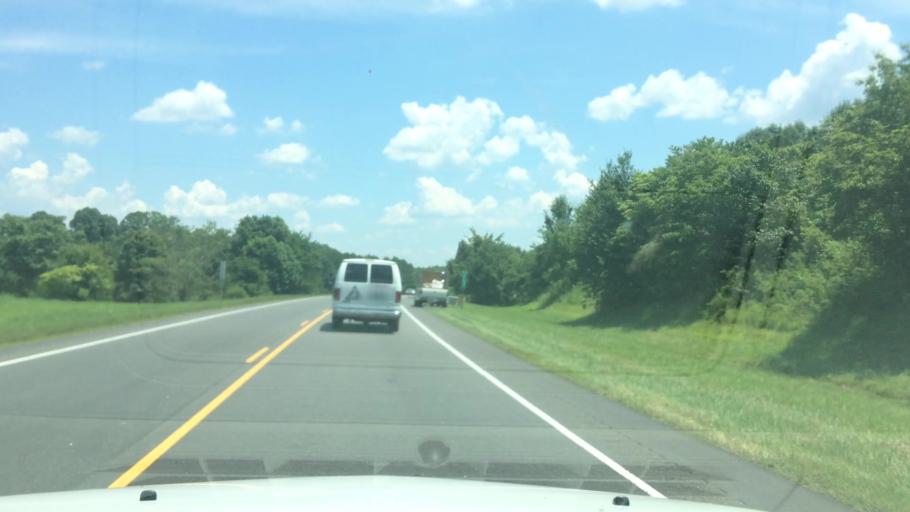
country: US
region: North Carolina
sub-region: Alexander County
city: Stony Point
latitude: 35.8153
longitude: -80.9871
